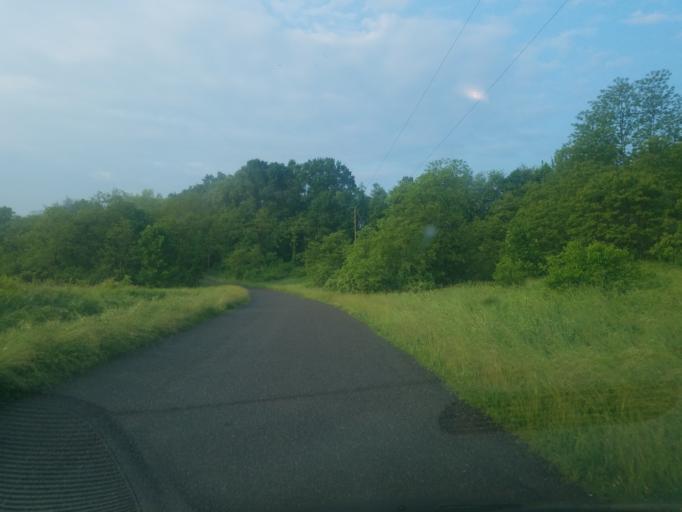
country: US
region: Ohio
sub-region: Stark County
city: Minerva
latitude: 40.7406
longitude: -80.9808
